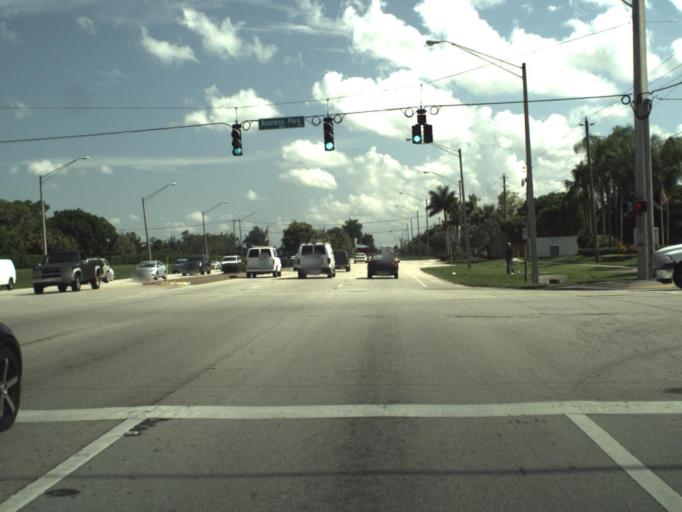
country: US
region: Florida
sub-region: Palm Beach County
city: Royal Palm Beach
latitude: 26.6996
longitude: -80.2014
